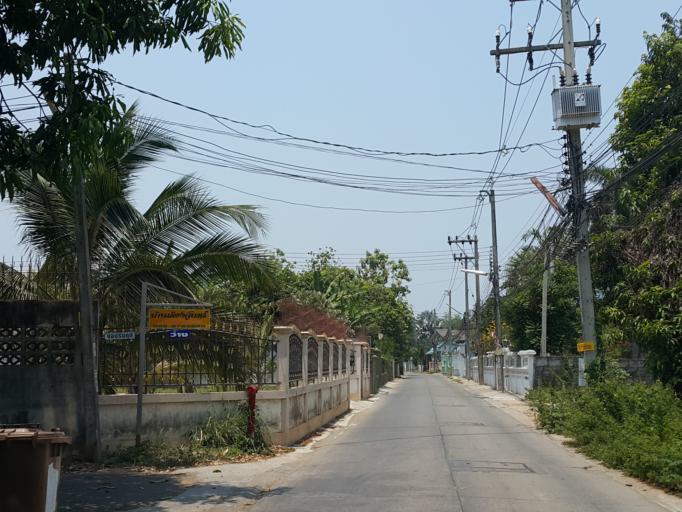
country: TH
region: Phitsanulok
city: Phitsanulok
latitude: 16.8158
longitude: 100.2497
